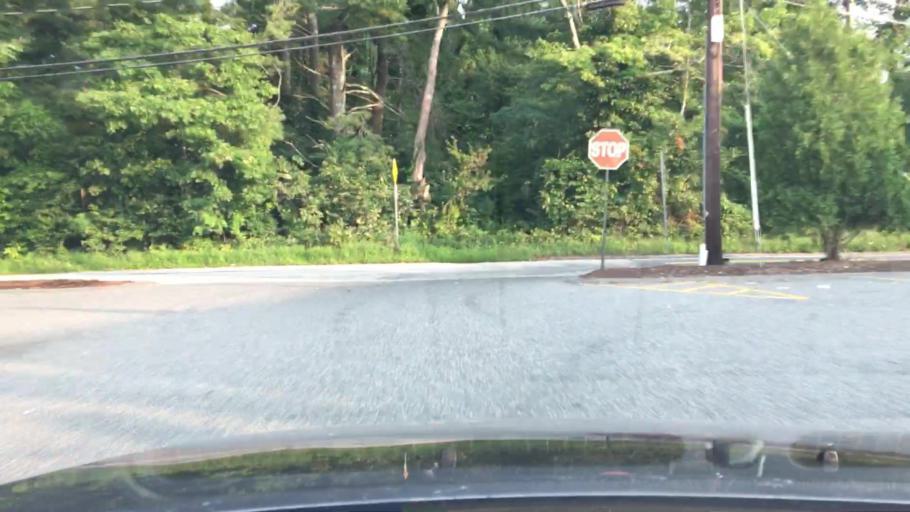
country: US
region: Massachusetts
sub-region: Middlesex County
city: Hopkinton
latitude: 42.2055
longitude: -71.5455
